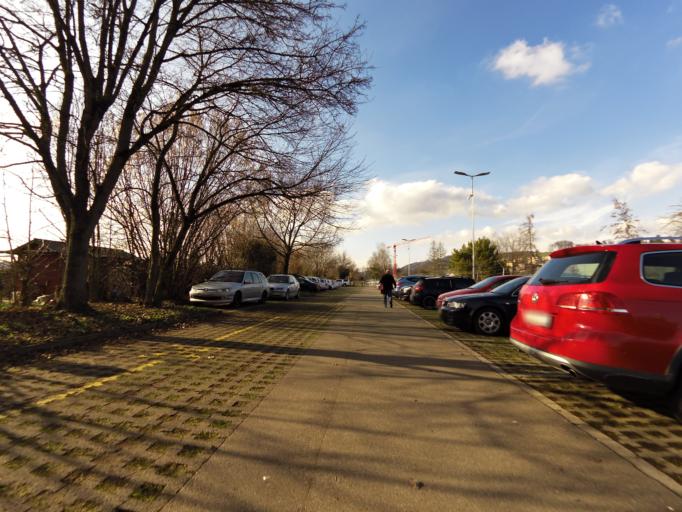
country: CH
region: Zurich
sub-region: Bezirk Zuerich
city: Zuerich (Kreis 9) / Altstetten
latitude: 47.4003
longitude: 8.4793
